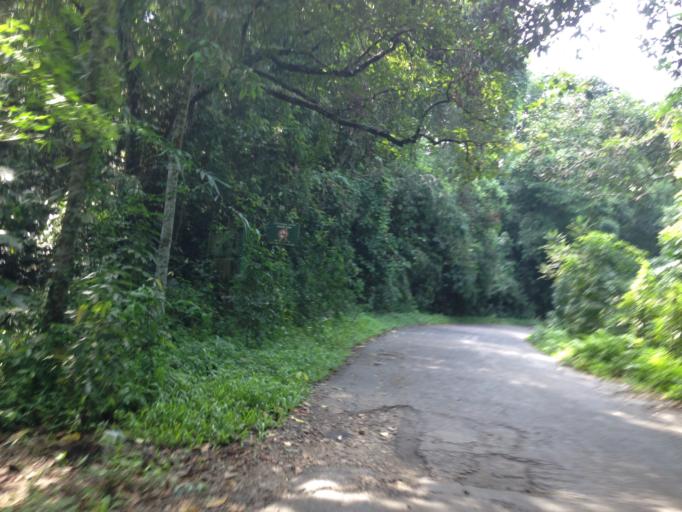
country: IN
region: Tripura
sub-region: Dhalai
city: Kamalpur
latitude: 24.3128
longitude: 91.7741
